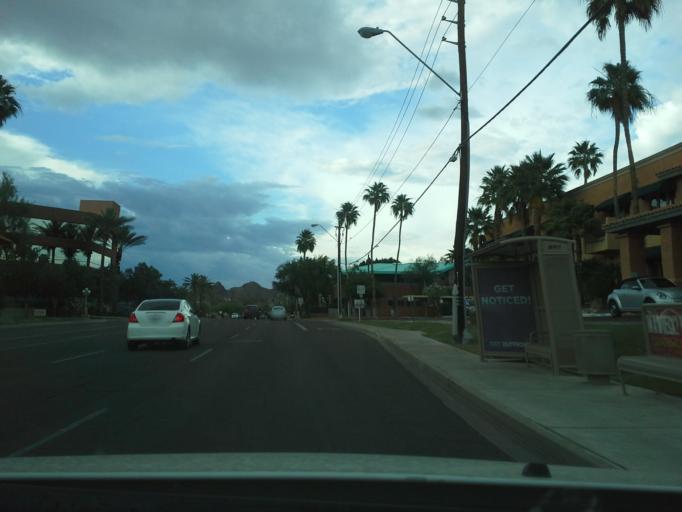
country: US
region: Arizona
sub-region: Maricopa County
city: Phoenix
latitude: 33.5422
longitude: -112.0474
